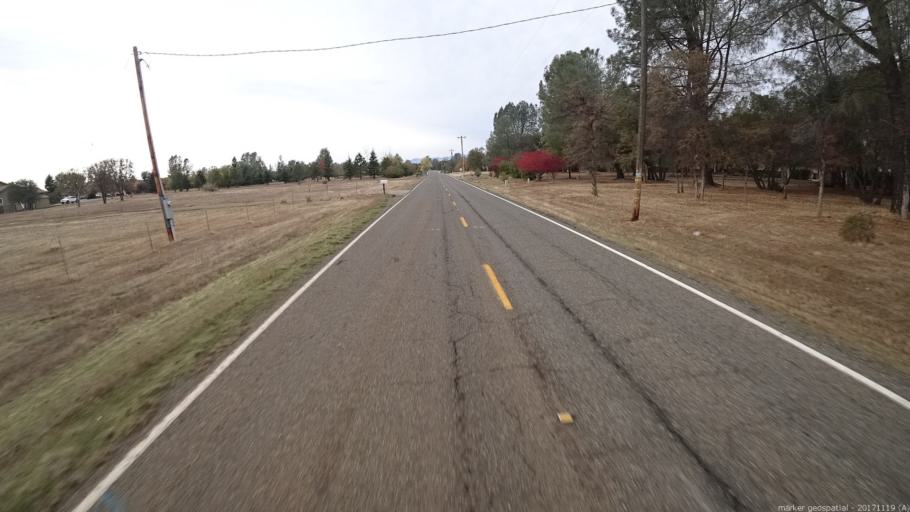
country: US
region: California
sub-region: Shasta County
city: Redding
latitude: 40.4882
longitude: -122.4318
